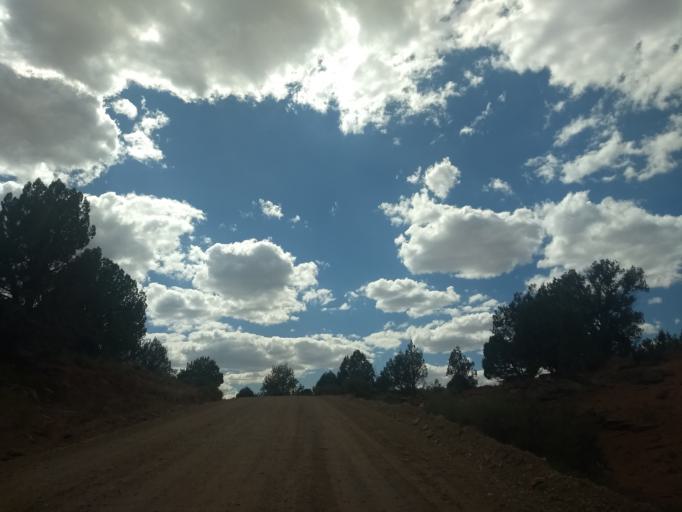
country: US
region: Utah
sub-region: Kane County
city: Kanab
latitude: 37.1520
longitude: -112.5428
